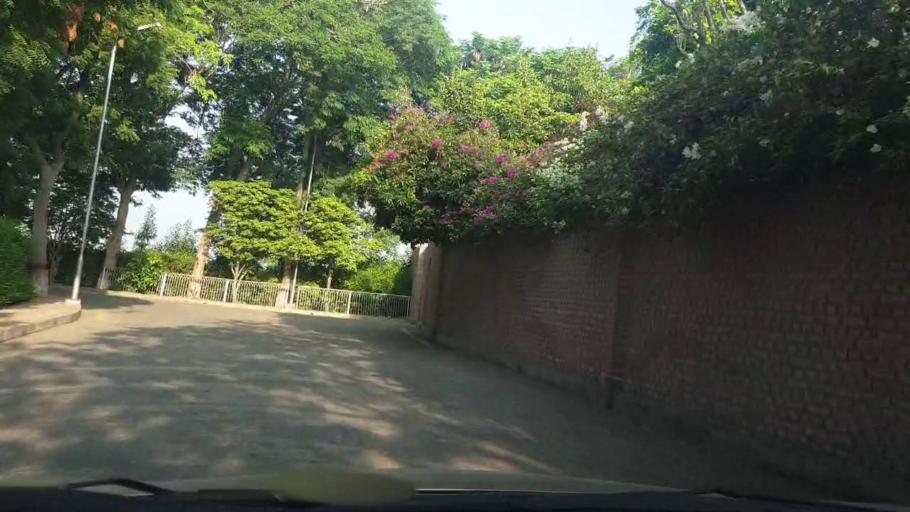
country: PK
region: Sindh
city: Larkana
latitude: 27.5783
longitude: 68.1760
